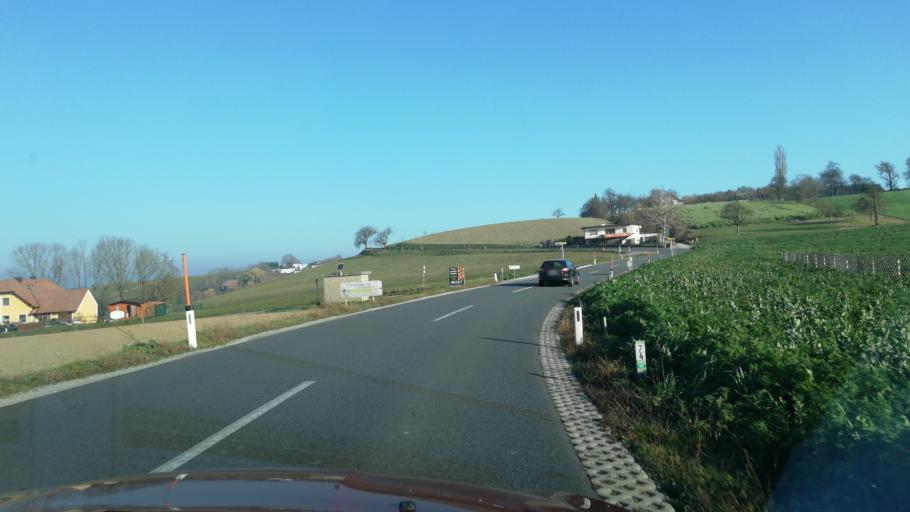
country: AT
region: Upper Austria
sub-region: Wels-Land
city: Buchkirchen
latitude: 48.2428
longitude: 14.0194
